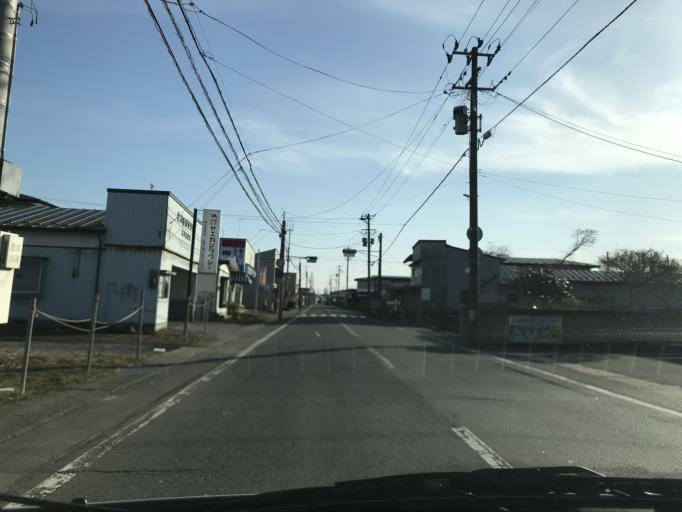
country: JP
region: Iwate
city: Kitakami
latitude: 39.2630
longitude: 141.1150
